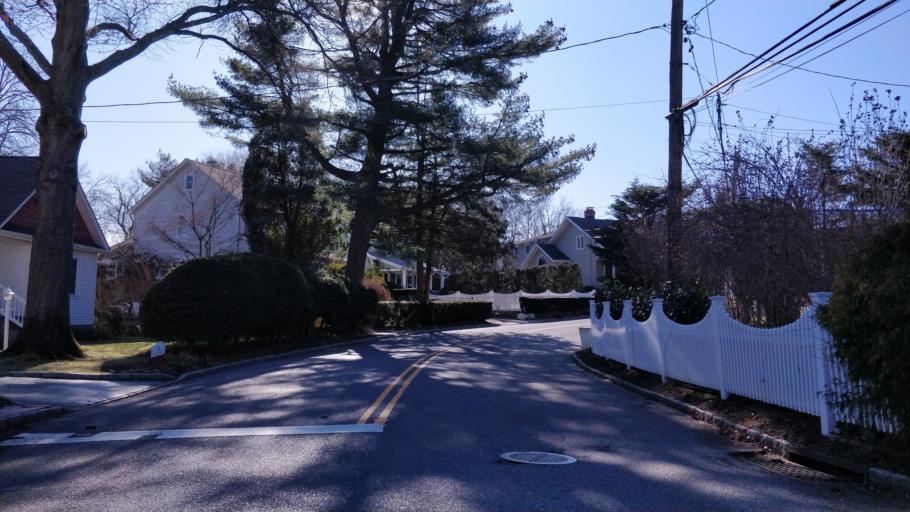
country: US
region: New York
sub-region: Nassau County
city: Glen Head
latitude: 40.8376
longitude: -73.6231
